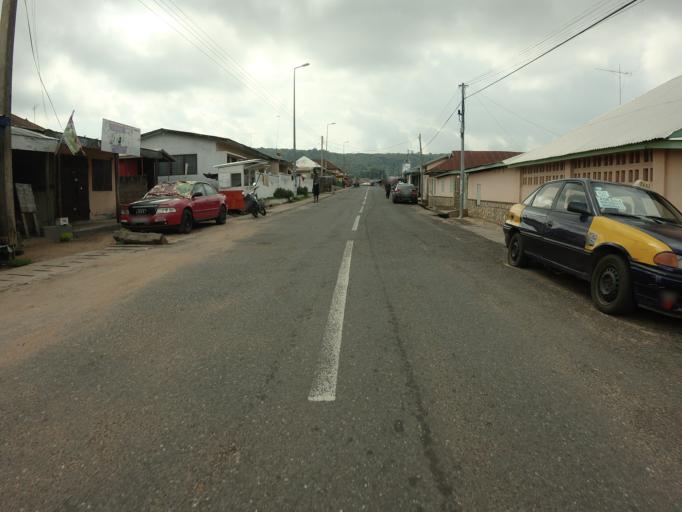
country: GH
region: Volta
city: Ho
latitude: 6.6128
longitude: 0.4676
